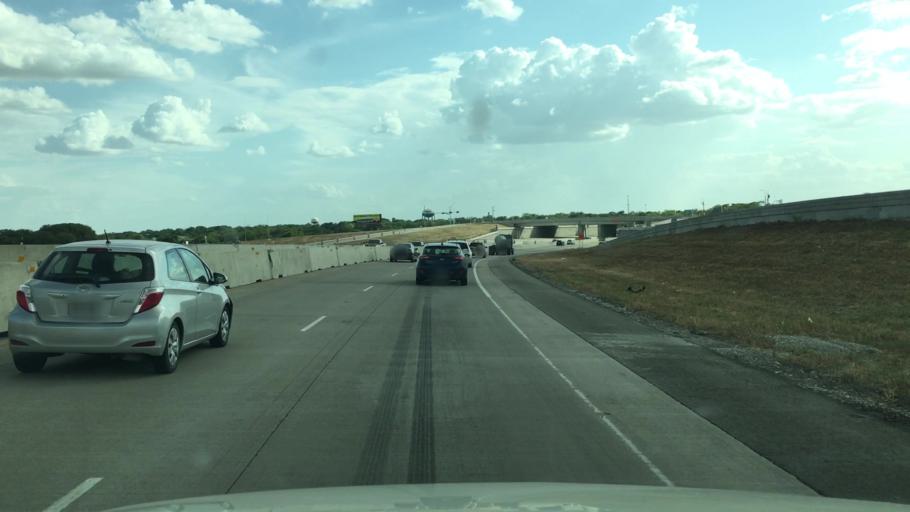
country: US
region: Texas
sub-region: Bell County
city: Temple
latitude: 31.1287
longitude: -97.3345
